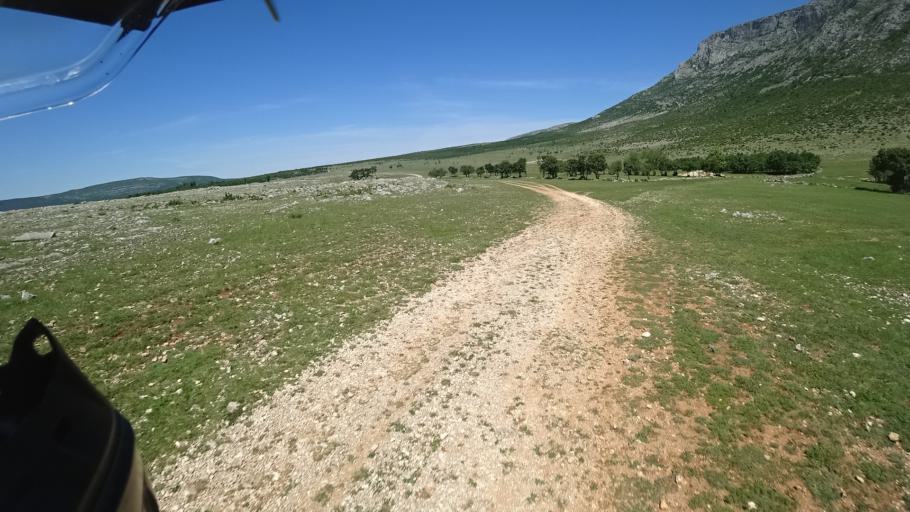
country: BA
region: Federation of Bosnia and Herzegovina
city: Bosansko Grahovo
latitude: 44.0025
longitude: 16.4010
